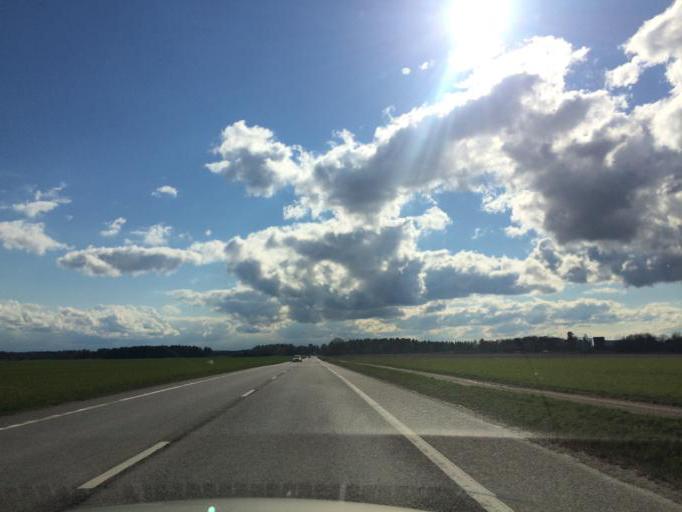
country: SE
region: Soedermanland
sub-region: Eskilstuna Kommun
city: Eskilstuna
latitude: 59.4206
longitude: 16.5982
